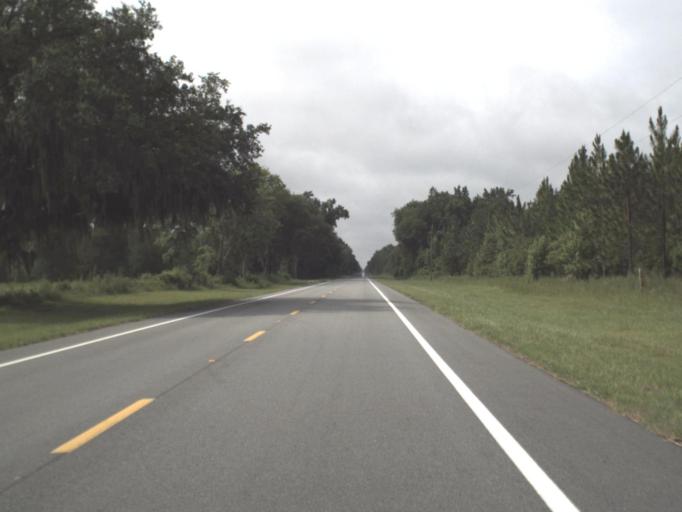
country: US
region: Florida
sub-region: Columbia County
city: Five Points
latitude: 30.4613
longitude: -82.6524
